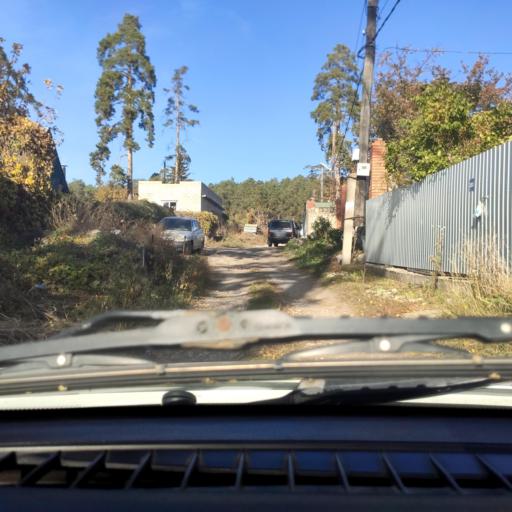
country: RU
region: Samara
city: Zhigulevsk
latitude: 53.4695
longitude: 49.5877
